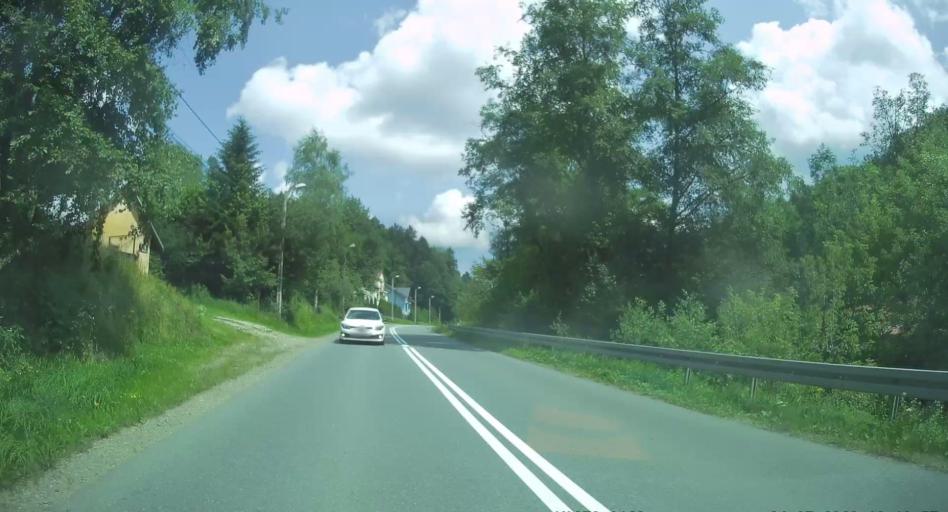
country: PL
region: Lesser Poland Voivodeship
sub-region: Powiat nowosadecki
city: Nowy Sacz
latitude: 49.6500
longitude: 20.7217
